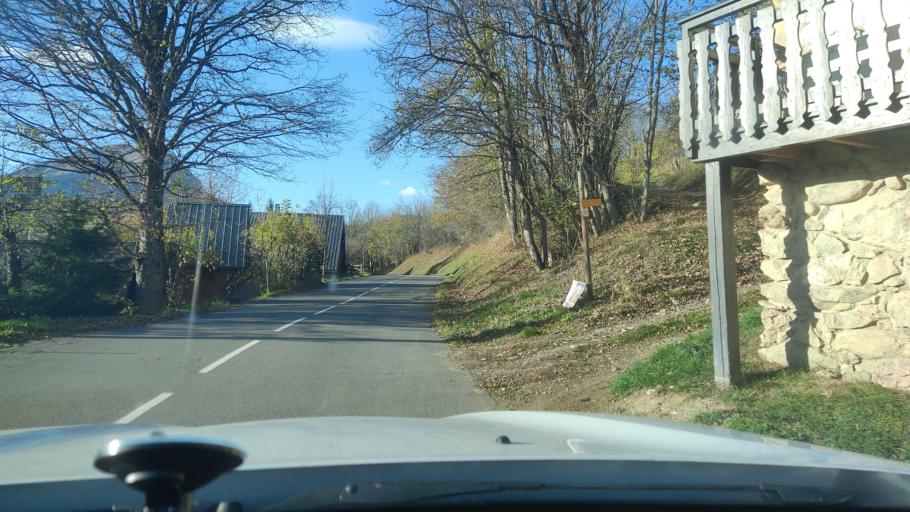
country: FR
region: Rhone-Alpes
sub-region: Departement de la Savoie
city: Saint-Jean-de-Maurienne
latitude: 45.2568
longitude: 6.3031
